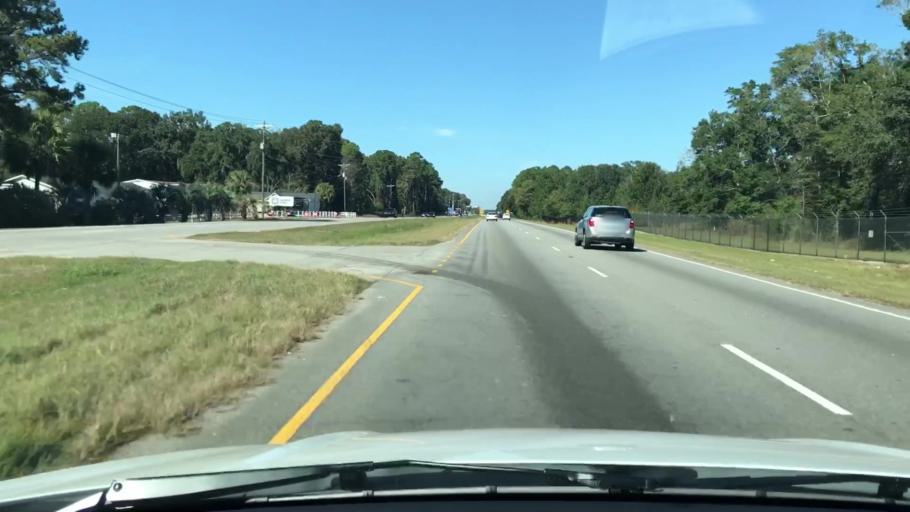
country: US
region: South Carolina
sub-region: Beaufort County
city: Burton
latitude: 32.4873
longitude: -80.7407
